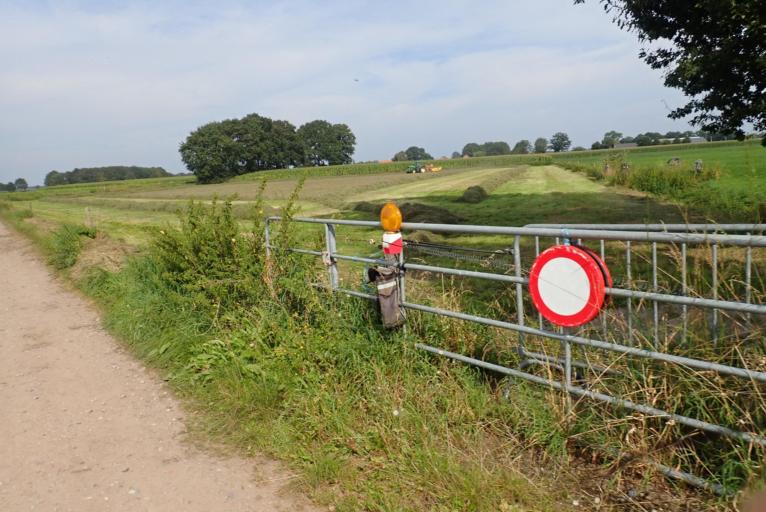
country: BE
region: Flanders
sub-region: Provincie Antwerpen
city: Essen
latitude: 51.4465
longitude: 4.3870
